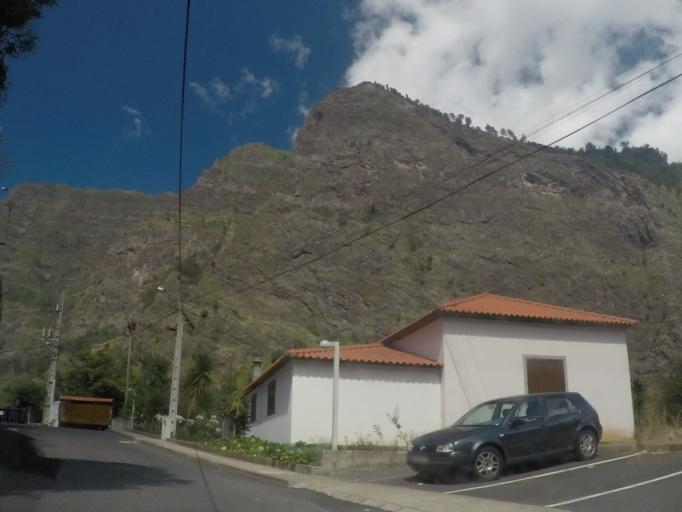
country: PT
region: Madeira
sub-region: Camara de Lobos
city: Curral das Freiras
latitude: 32.7087
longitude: -16.9736
